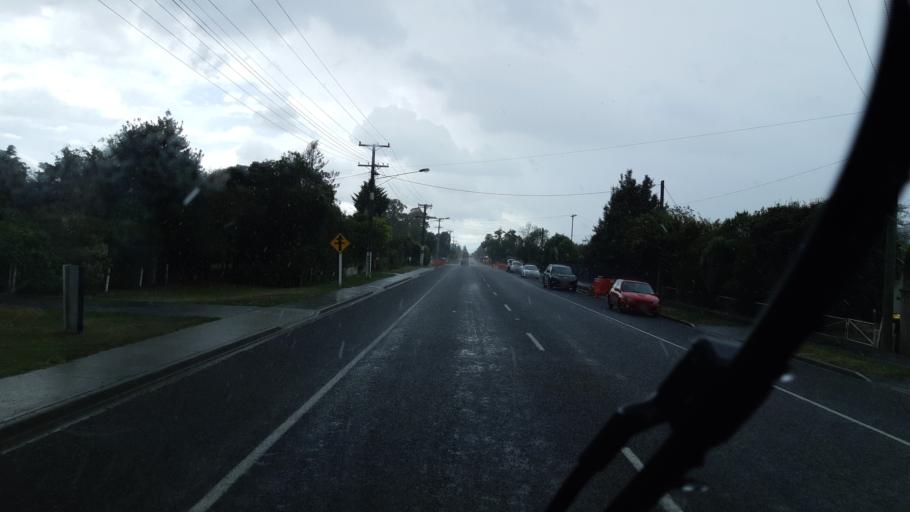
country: NZ
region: Tasman
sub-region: Tasman District
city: Wakefield
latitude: -41.4000
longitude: 173.0583
